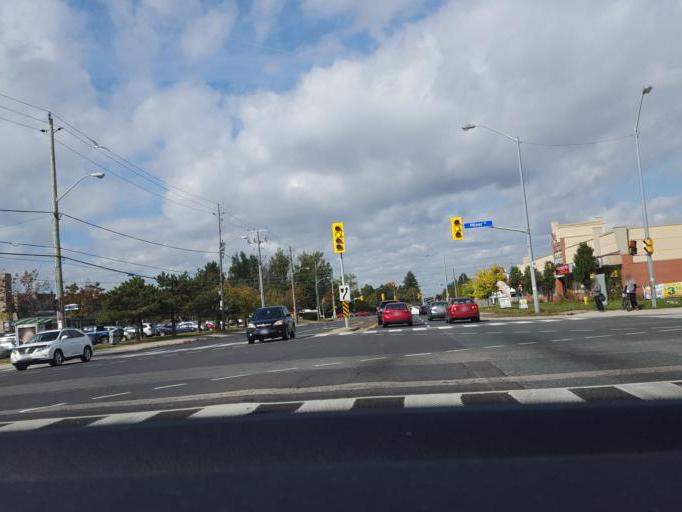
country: CA
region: Ontario
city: Scarborough
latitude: 43.8001
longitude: -79.1989
